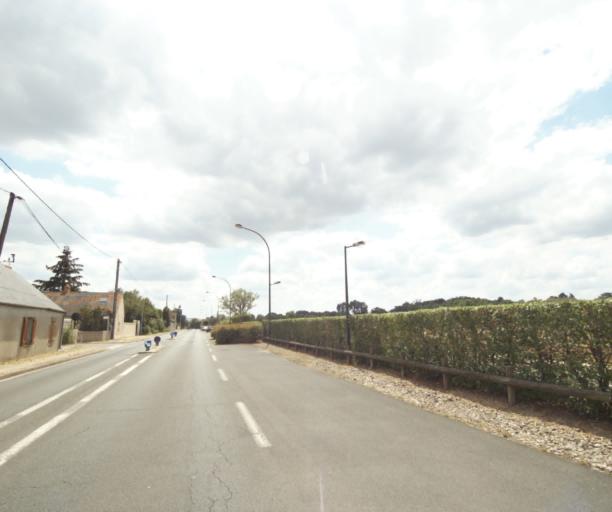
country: FR
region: Centre
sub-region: Departement du Loiret
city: Saint-Cyr-en-Val
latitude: 47.8350
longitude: 1.9606
